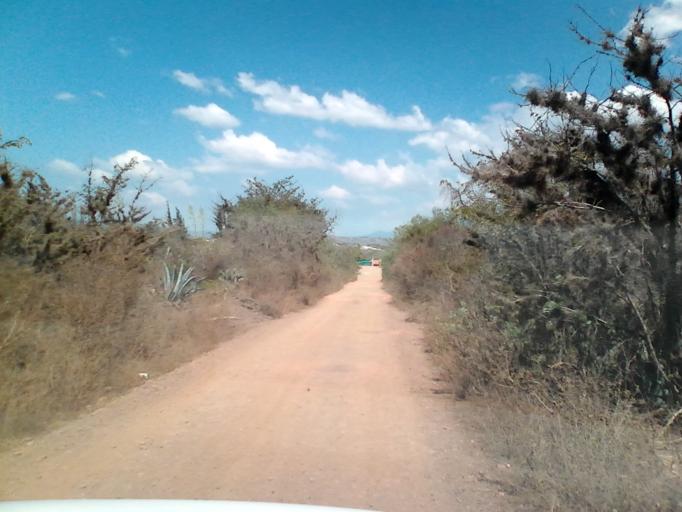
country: CO
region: Boyaca
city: Villa de Leiva
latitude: 5.6272
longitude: -73.5849
